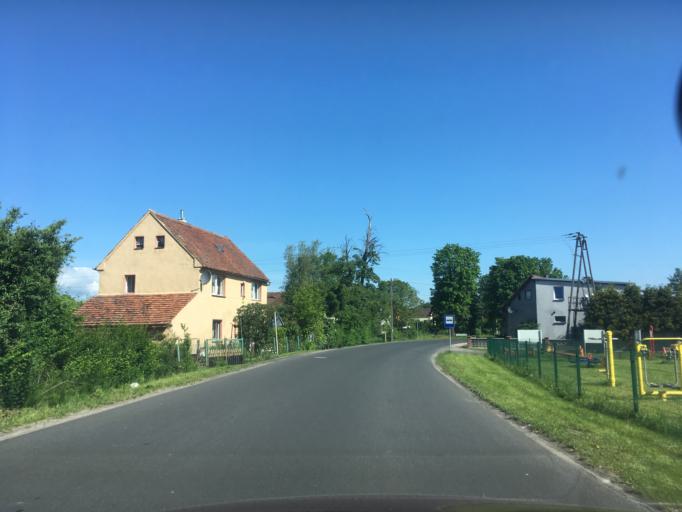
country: PL
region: Lower Silesian Voivodeship
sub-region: Powiat zgorzelecki
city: Sulikow
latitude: 51.0828
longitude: 15.0563
